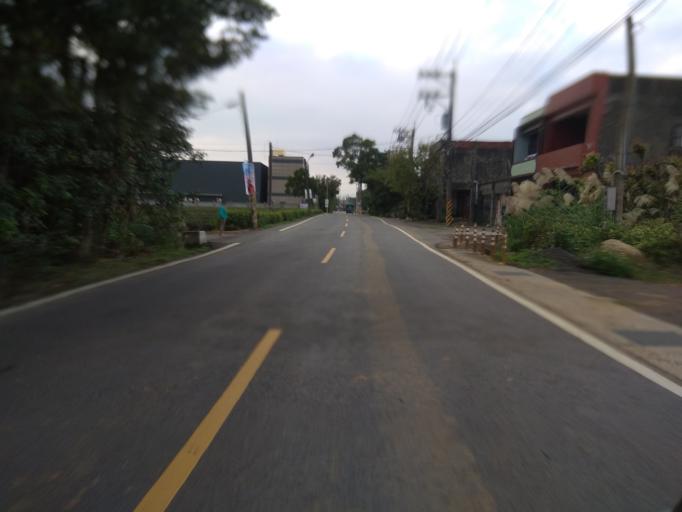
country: TW
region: Taiwan
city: Daxi
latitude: 24.8434
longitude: 121.2016
